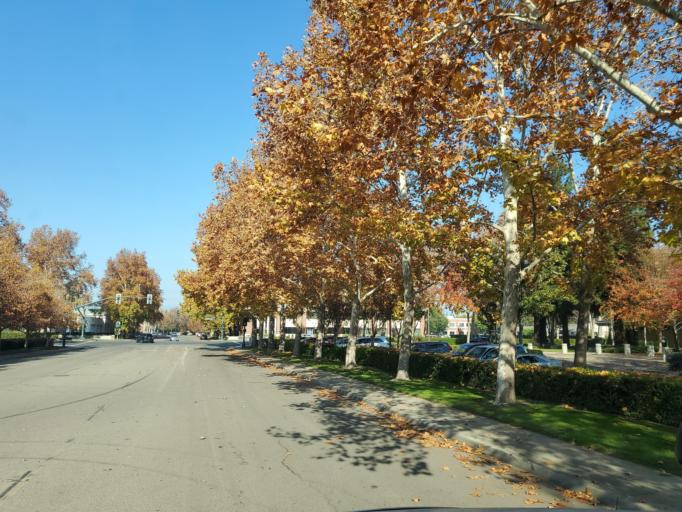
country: US
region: California
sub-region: San Joaquin County
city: Country Club
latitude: 37.9830
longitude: -121.3523
